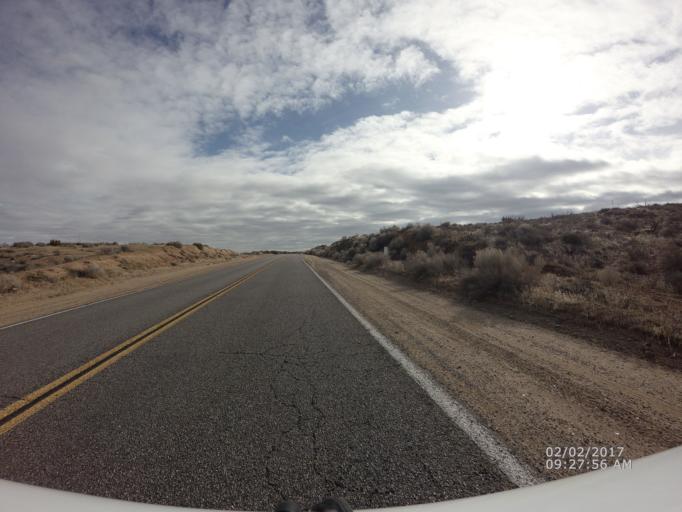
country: US
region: California
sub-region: Los Angeles County
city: Vincent
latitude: 34.5282
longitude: -118.0650
